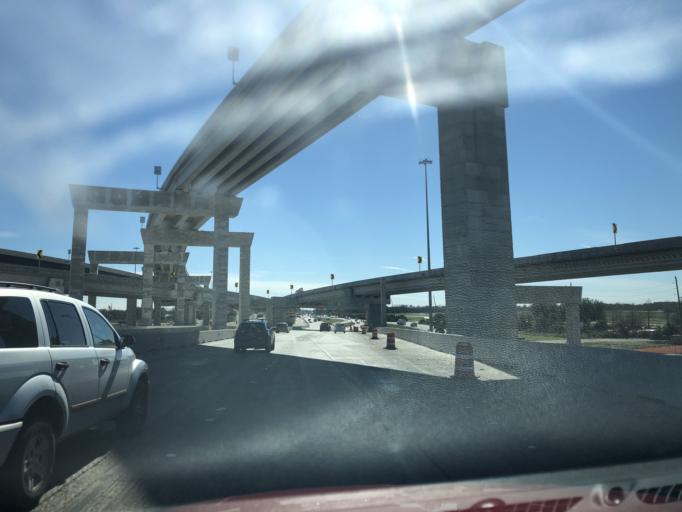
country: US
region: Texas
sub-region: Brazoria County
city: Brookside Village
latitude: 29.5961
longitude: -95.3868
